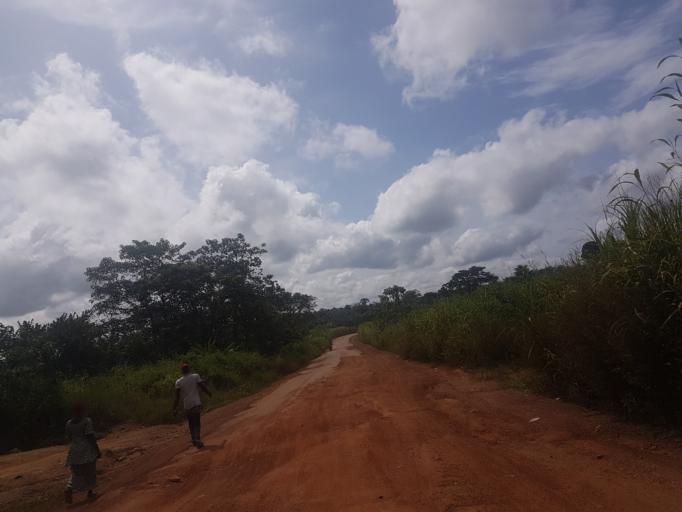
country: GN
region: Nzerekore
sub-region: Prefecture de Guekedou
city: Gueckedou
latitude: 8.6769
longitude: -10.1212
